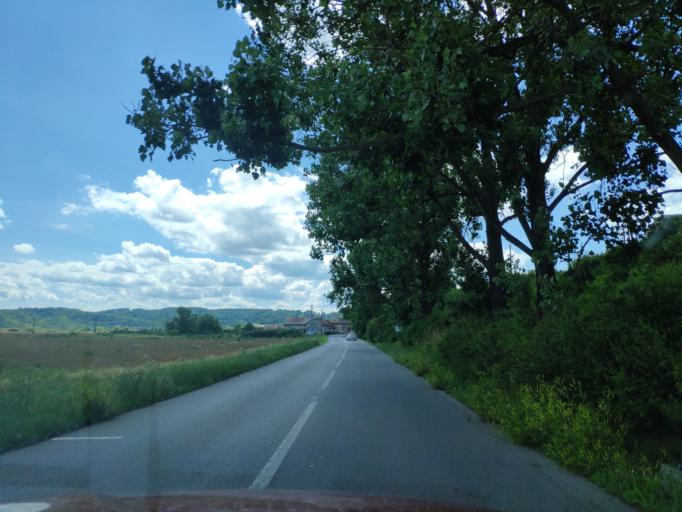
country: HU
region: Borsod-Abauj-Zemplen
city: Ozd
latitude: 48.3059
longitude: 20.2462
